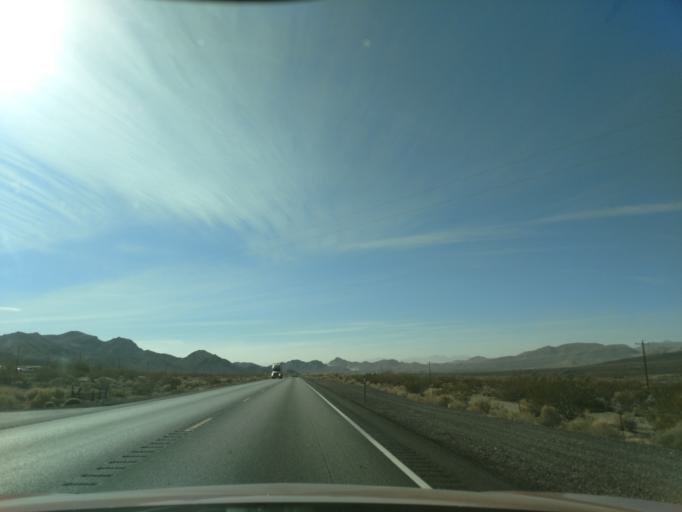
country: US
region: Nevada
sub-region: Nye County
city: Beatty
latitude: 36.9379
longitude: -116.7250
